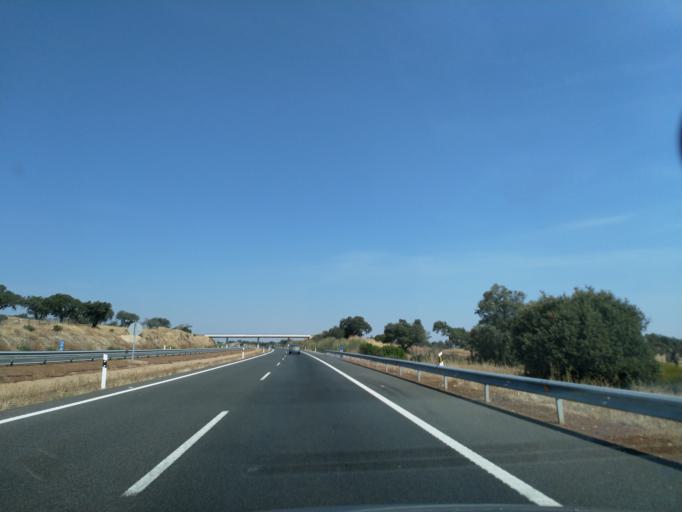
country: ES
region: Extremadura
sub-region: Provincia de Badajoz
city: Aljucen
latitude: 39.0087
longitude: -6.3303
